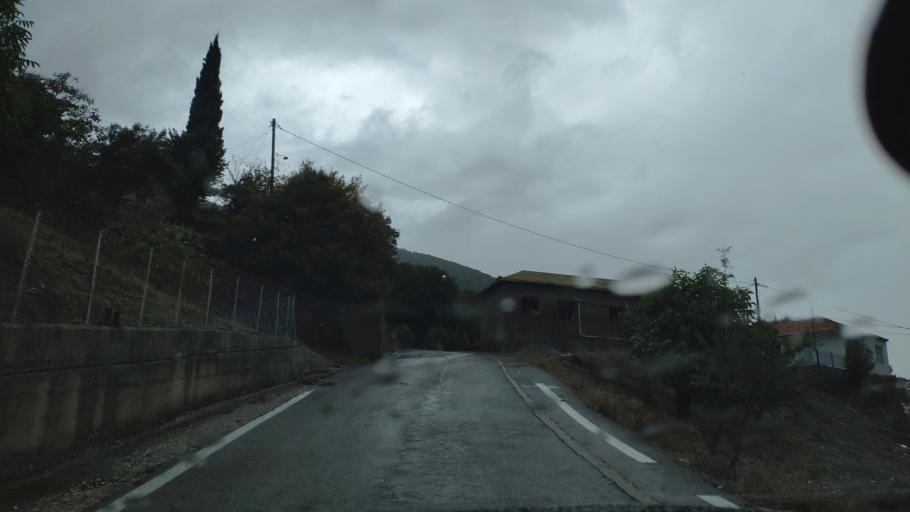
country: GR
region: Thessaly
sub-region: Nomos Kardhitsas
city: Anthiro
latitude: 39.1075
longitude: 21.4117
